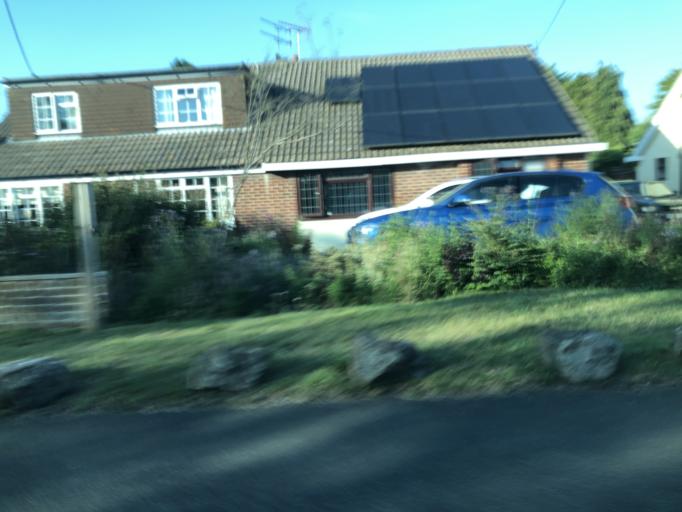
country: GB
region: England
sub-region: Kent
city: Meopham
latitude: 51.3439
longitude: 0.3476
